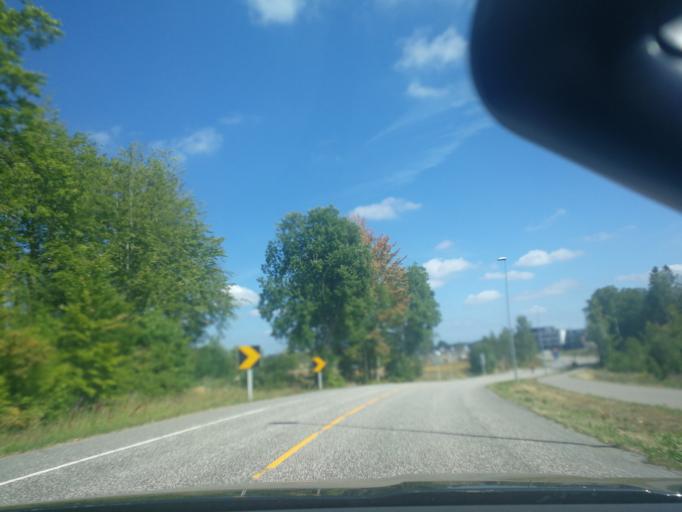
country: NO
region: Vestfold
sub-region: Stokke
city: Stokke
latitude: 59.2061
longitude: 10.2384
